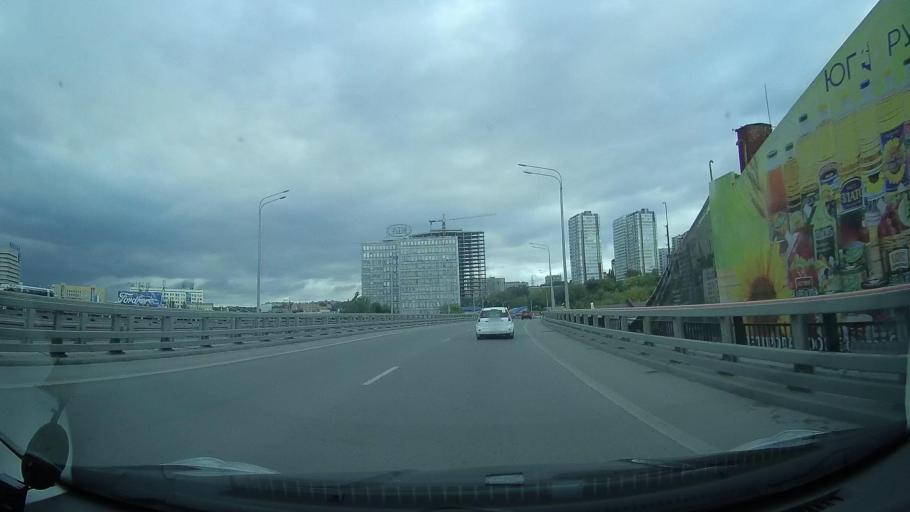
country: RU
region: Rostov
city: Rostov-na-Donu
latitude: 47.2182
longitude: 39.6954
